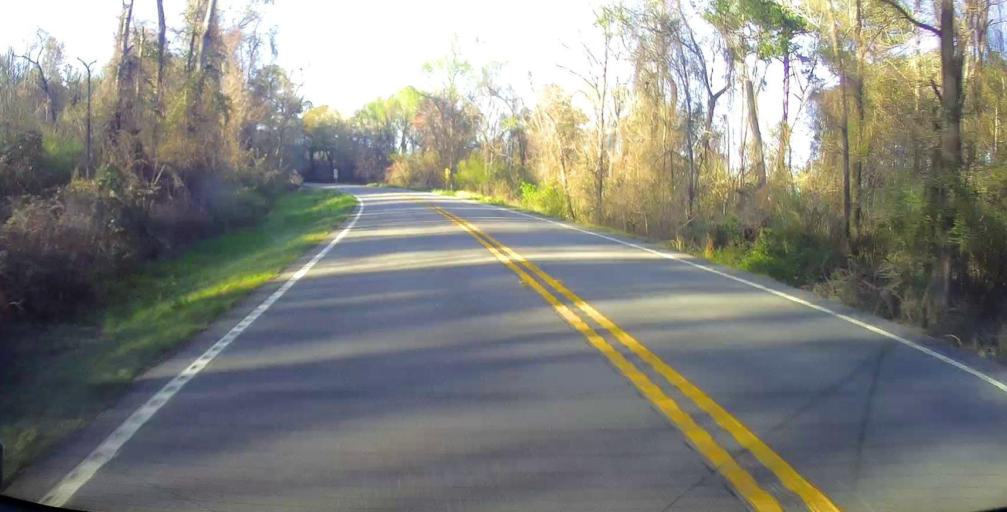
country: US
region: Georgia
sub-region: Pulaski County
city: Hawkinsville
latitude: 32.1772
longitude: -83.3609
